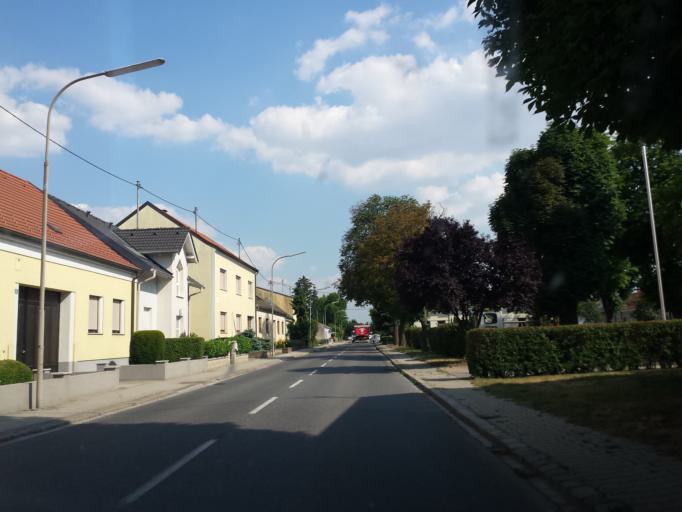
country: AT
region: Lower Austria
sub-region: Politischer Bezirk Ganserndorf
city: Markgrafneusiedl
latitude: 48.2662
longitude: 16.6332
